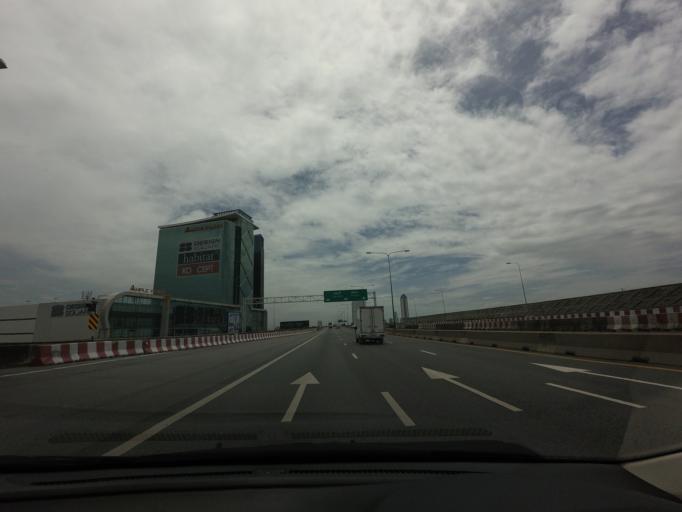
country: TH
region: Bangkok
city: Bang Na
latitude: 13.6665
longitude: 100.6412
